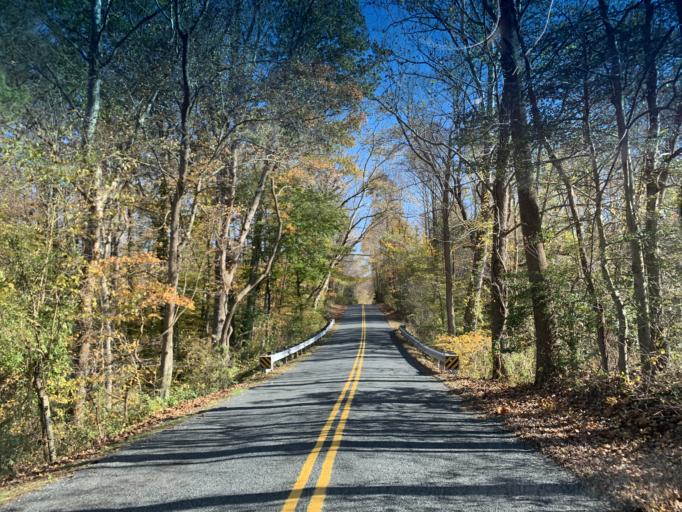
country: US
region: Maryland
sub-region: Harford County
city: Joppatowne
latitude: 39.4799
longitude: -76.3465
